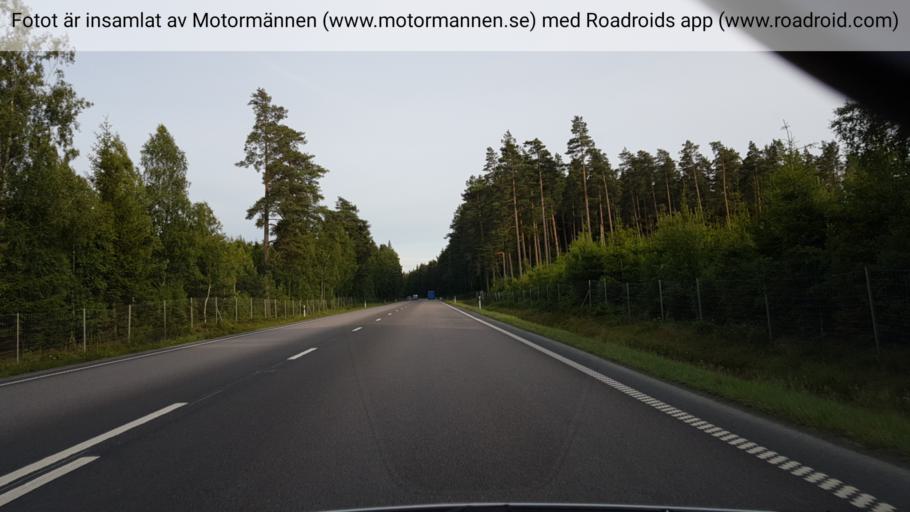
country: SE
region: Vaestra Goetaland
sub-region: Lidkopings Kommun
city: Lidkoping
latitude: 58.4733
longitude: 13.2086
